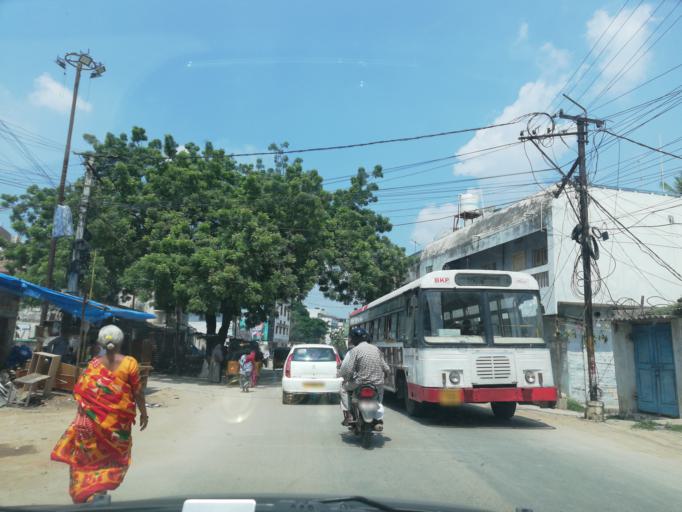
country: IN
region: Telangana
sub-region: Medak
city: Serilingampalle
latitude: 17.4903
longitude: 78.3183
